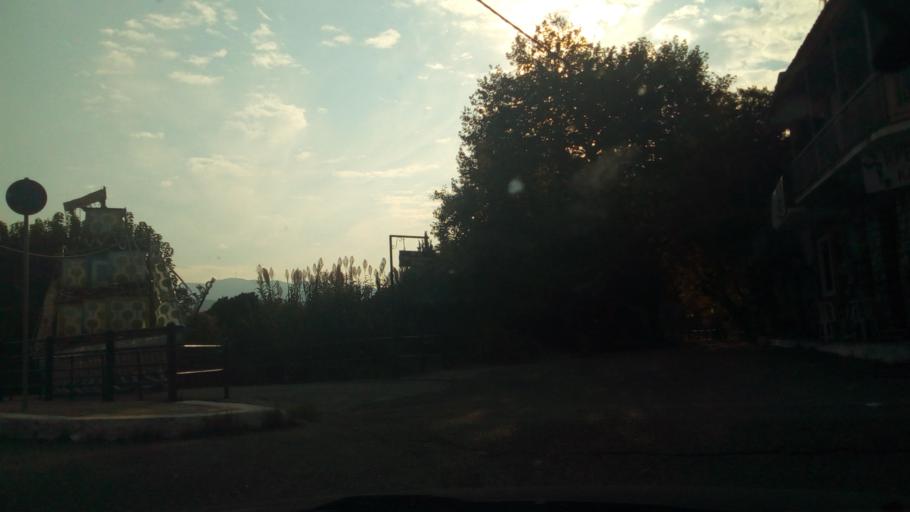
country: GR
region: West Greece
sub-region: Nomos Aitolias kai Akarnanias
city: Nafpaktos
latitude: 38.4198
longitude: 21.9280
